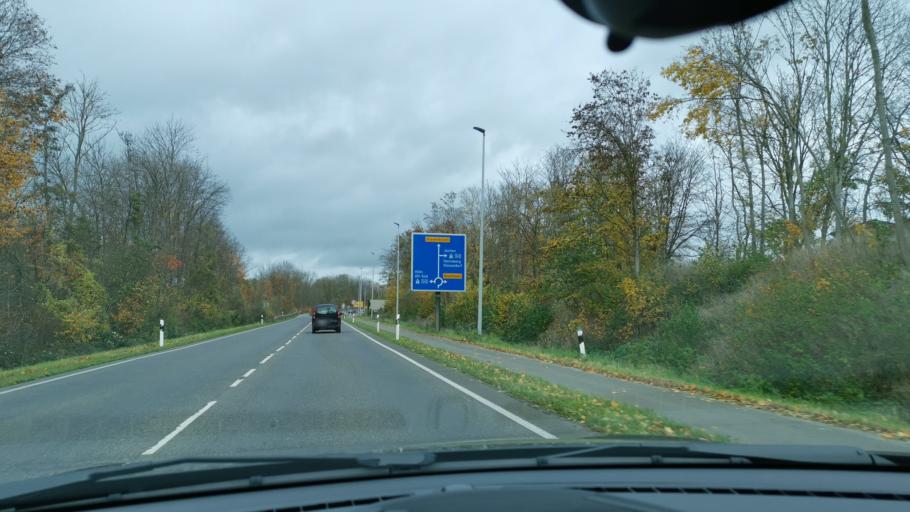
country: DE
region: North Rhine-Westphalia
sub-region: Regierungsbezirk Dusseldorf
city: Grevenbroich
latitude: 51.0725
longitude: 6.5876
